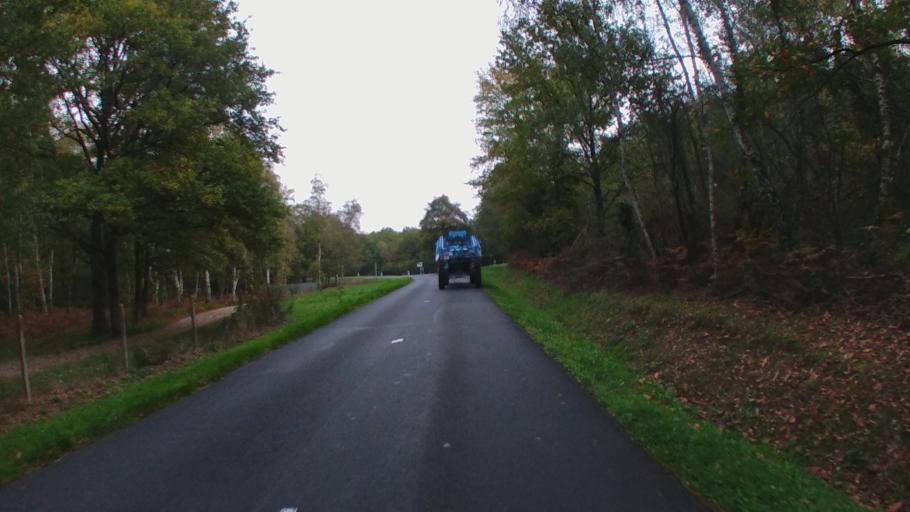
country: FR
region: Pays de la Loire
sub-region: Departement de Maine-et-Loire
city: Distre
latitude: 47.2561
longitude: -0.1313
